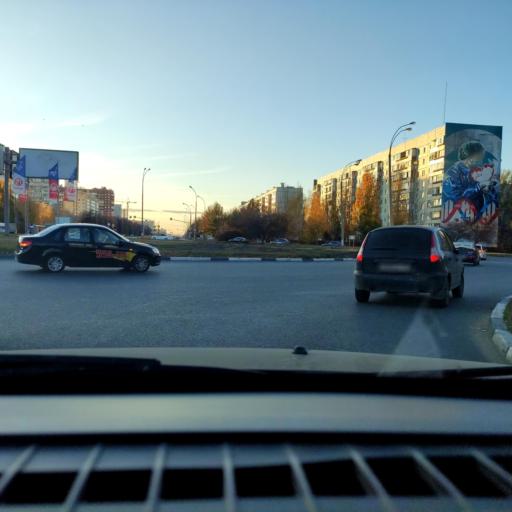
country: RU
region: Samara
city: Tol'yatti
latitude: 53.5263
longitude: 49.3128
